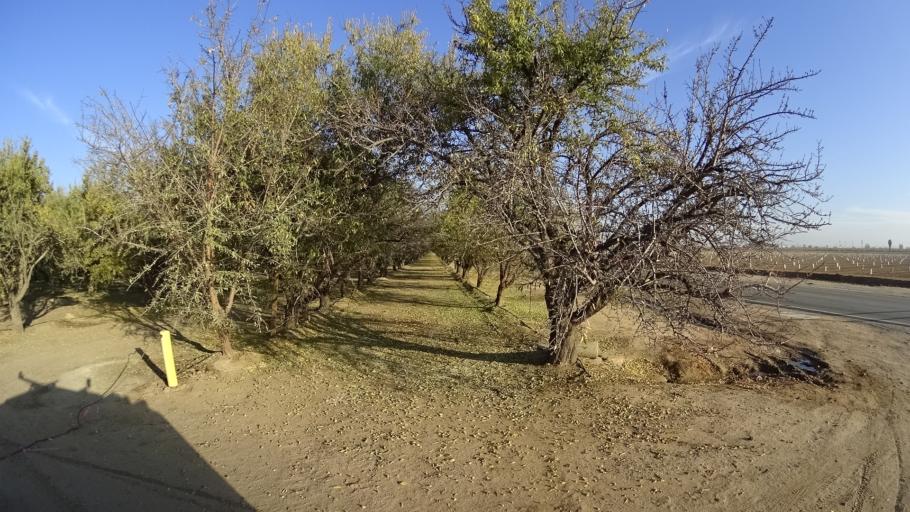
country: US
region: California
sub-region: Kern County
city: Greenacres
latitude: 35.4343
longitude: -119.0924
